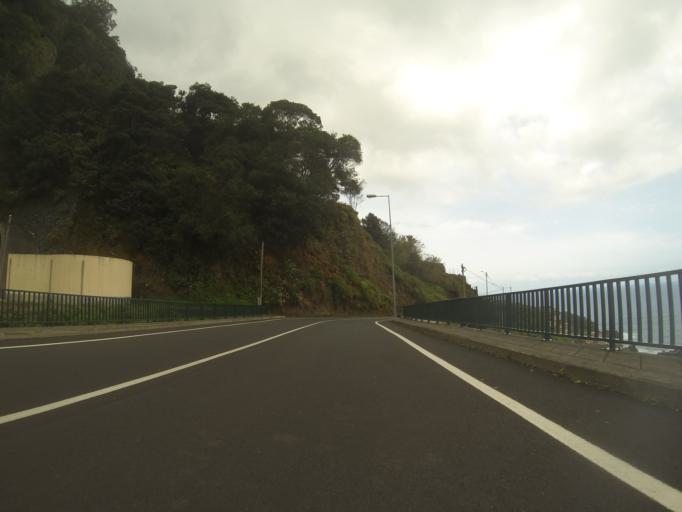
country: PT
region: Madeira
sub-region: Sao Vicente
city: Sao Vicente
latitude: 32.8200
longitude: -17.1037
